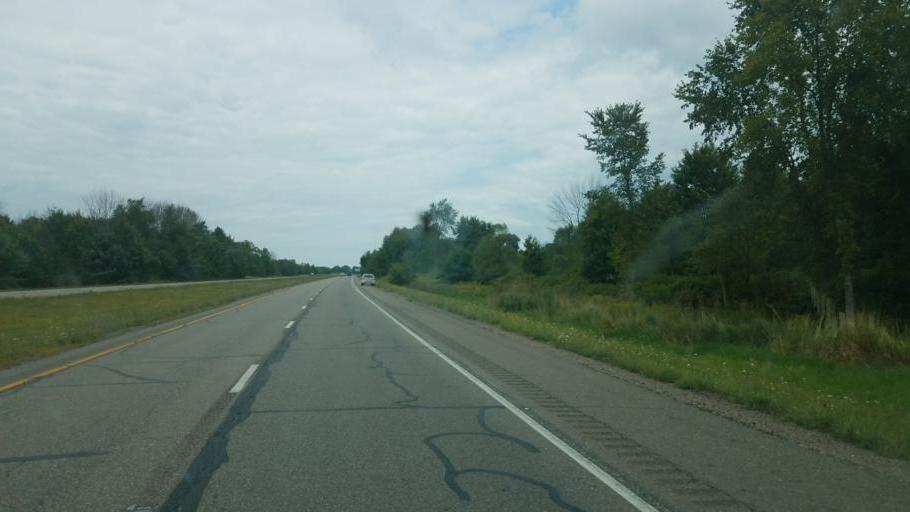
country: US
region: Ohio
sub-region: Columbiana County
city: Lisbon
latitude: 40.8164
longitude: -80.7454
